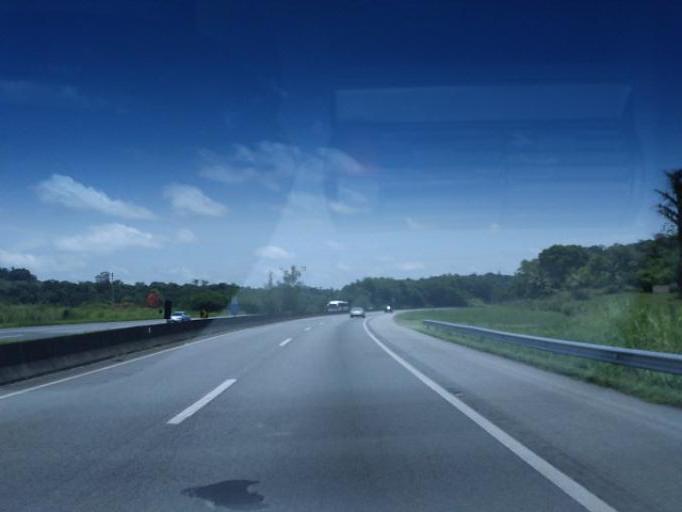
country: BR
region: Sao Paulo
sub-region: Juquia
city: Juquia
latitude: -24.3343
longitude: -47.5917
